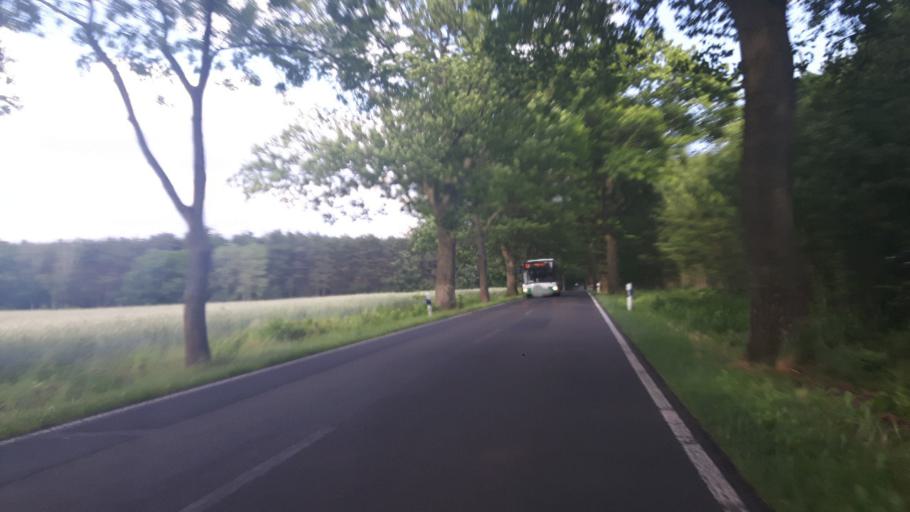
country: DE
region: Brandenburg
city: Melchow
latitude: 52.7491
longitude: 13.7502
